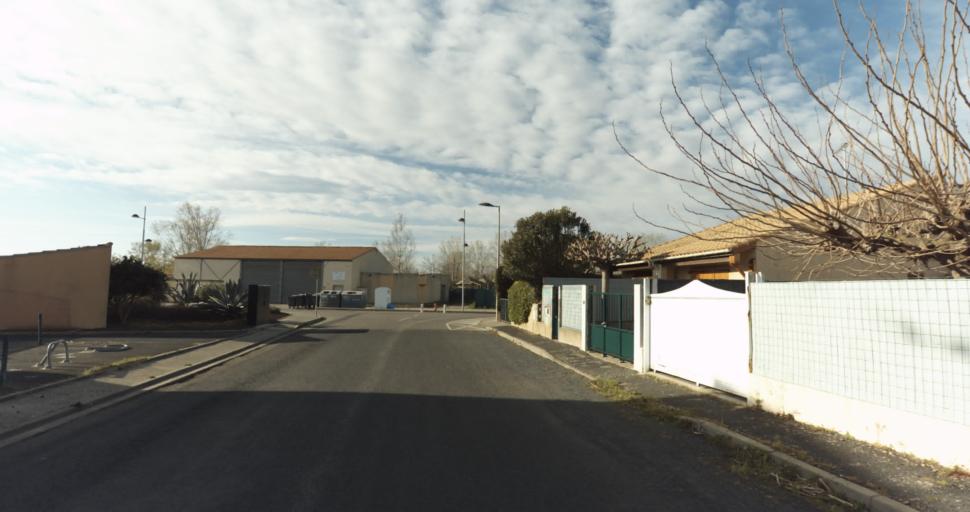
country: FR
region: Languedoc-Roussillon
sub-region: Departement de l'Herault
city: Marseillan
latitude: 43.3163
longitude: 3.5455
